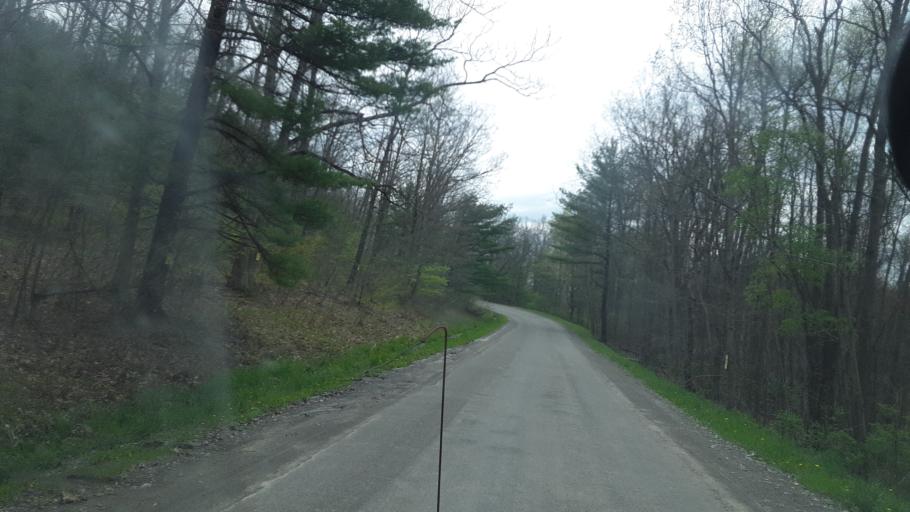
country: US
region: New York
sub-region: Steuben County
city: Addison
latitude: 42.0941
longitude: -77.3133
